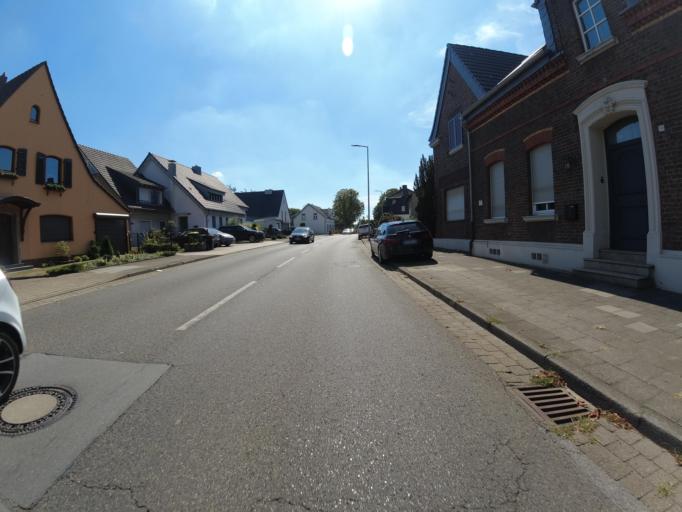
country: DE
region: North Rhine-Westphalia
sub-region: Regierungsbezirk Dusseldorf
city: Moers
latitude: 51.4876
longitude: 6.6709
